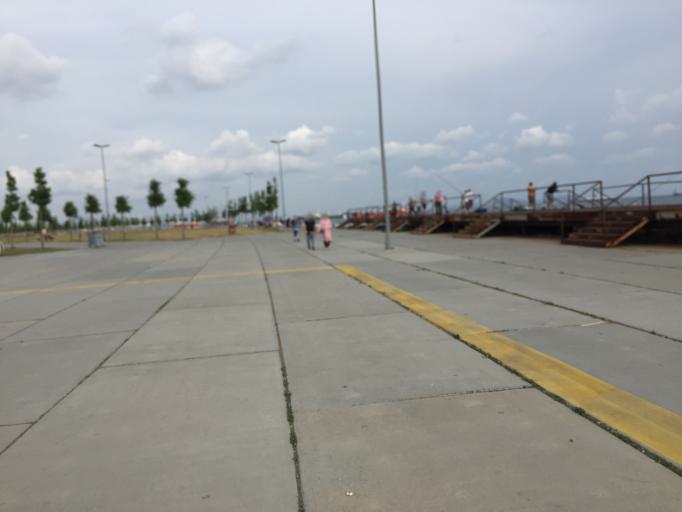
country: TR
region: Istanbul
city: Istanbul
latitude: 40.9971
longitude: 28.9422
